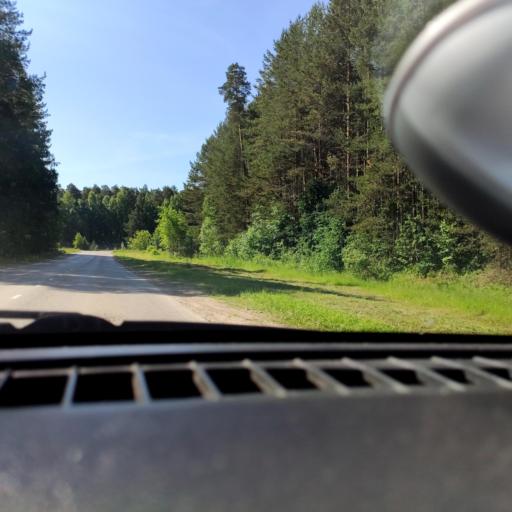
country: RU
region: Perm
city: Overyata
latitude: 57.9955
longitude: 55.8821
